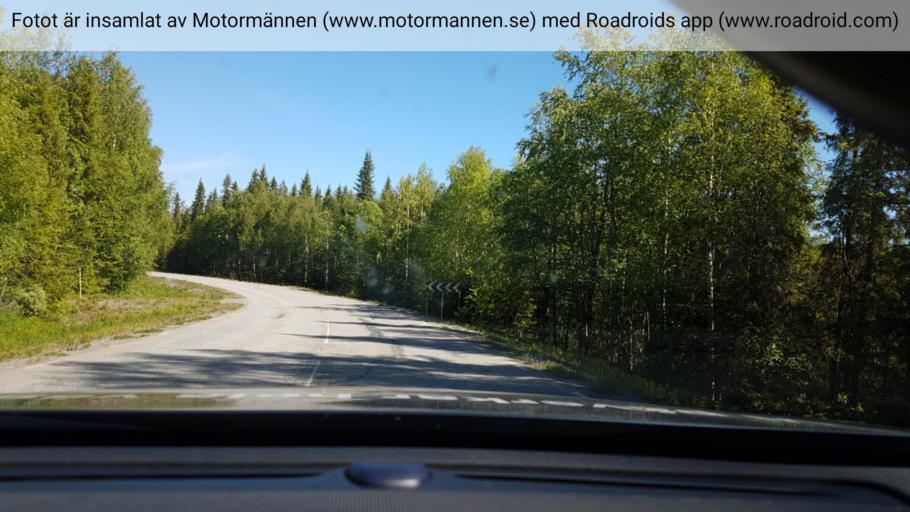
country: SE
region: Vaesterbotten
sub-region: Vilhelmina Kommun
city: Vilhelmina
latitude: 64.6273
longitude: 16.7606
